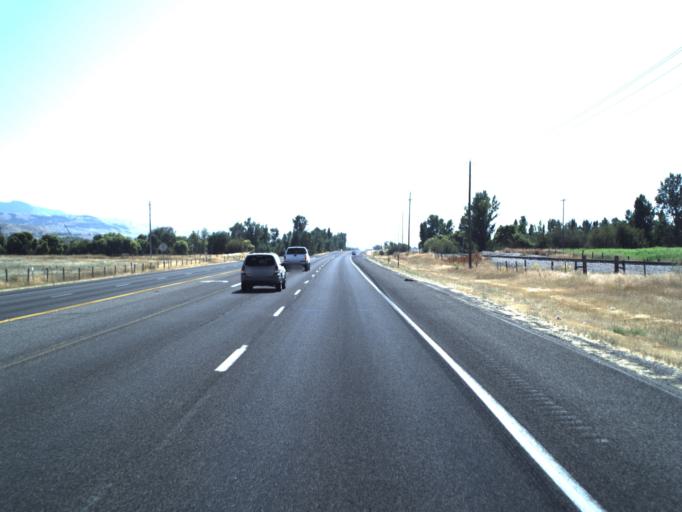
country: US
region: Utah
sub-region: Cache County
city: Richmond
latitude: 41.9610
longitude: -111.8130
